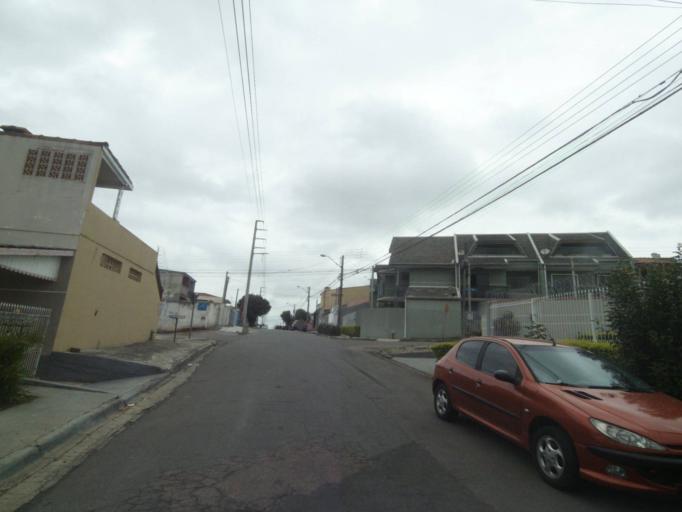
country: BR
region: Parana
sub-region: Sao Jose Dos Pinhais
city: Sao Jose dos Pinhais
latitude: -25.5438
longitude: -49.2690
